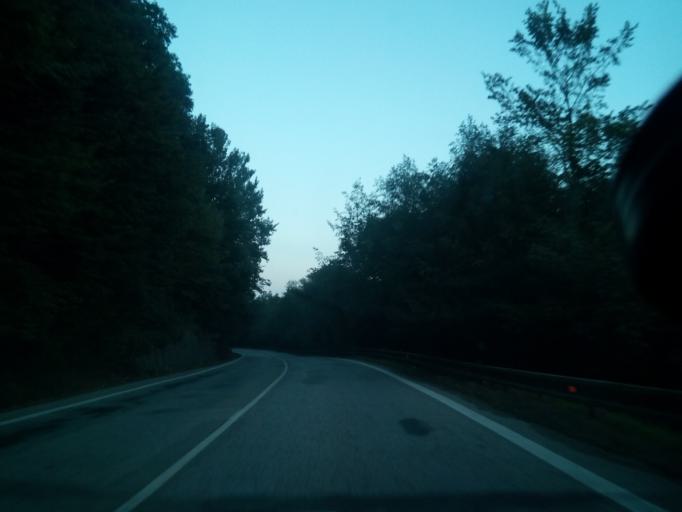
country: SK
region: Kosicky
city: Dobsina
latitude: 48.7996
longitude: 20.3870
